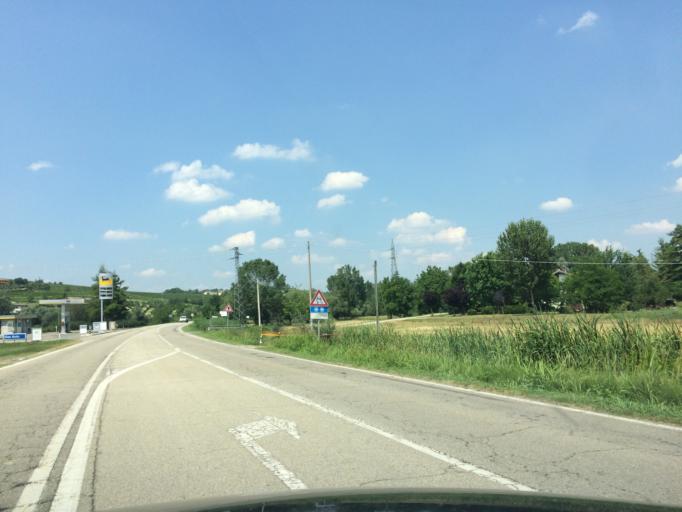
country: IT
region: Piedmont
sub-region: Provincia di Asti
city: Moasca
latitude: 44.7675
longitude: 8.2692
